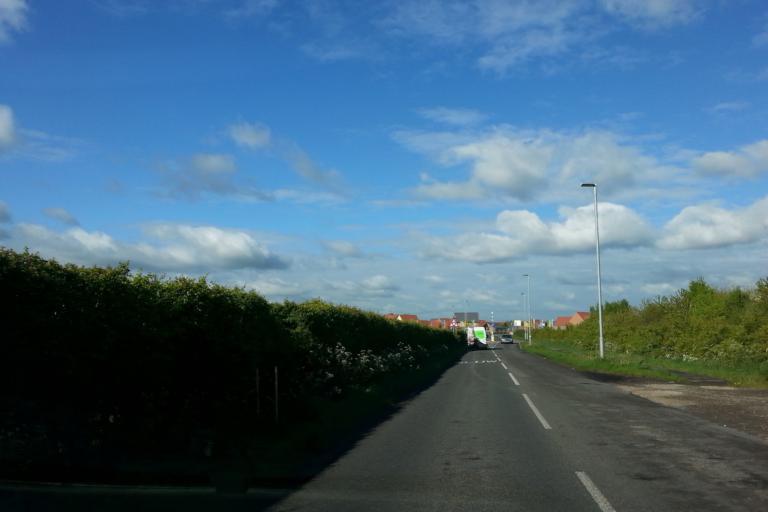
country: GB
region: England
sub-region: Nottinghamshire
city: Cotgrave
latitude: 52.9193
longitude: -1.0244
